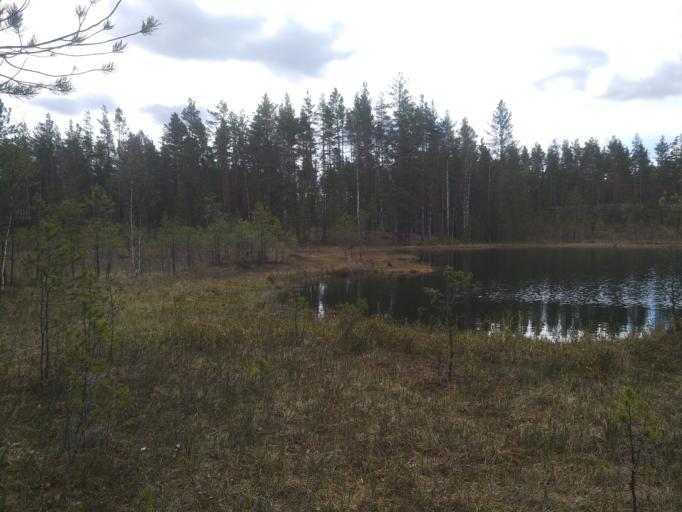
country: RU
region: Leningrad
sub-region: Vsevolzhskij Rajon
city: Vaskelovo
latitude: 60.5141
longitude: 30.4637
